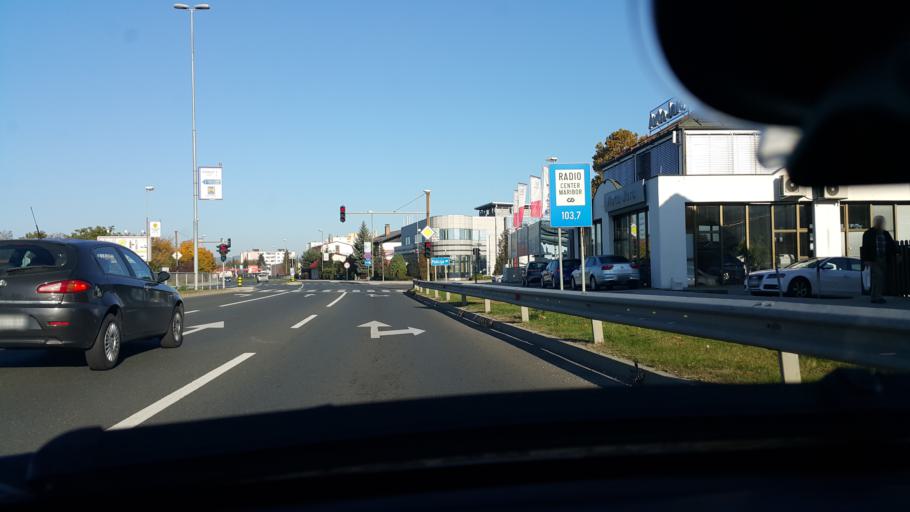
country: SI
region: Hoce-Slivnica
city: Rogoza
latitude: 46.5300
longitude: 15.6712
